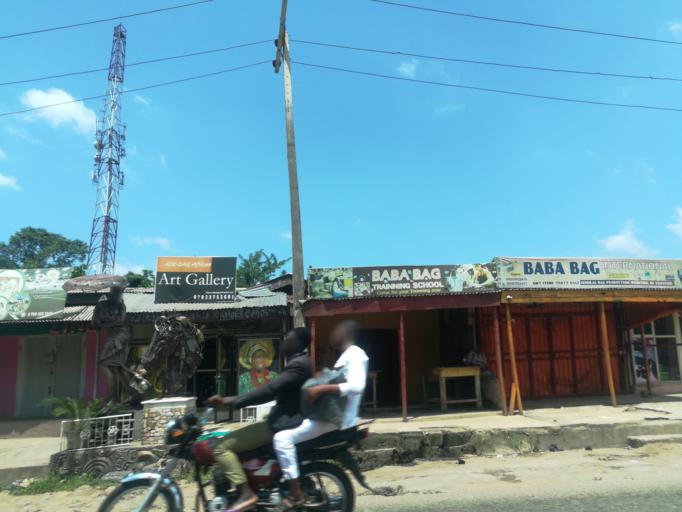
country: NG
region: Oyo
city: Ibadan
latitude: 7.3834
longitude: 3.8731
